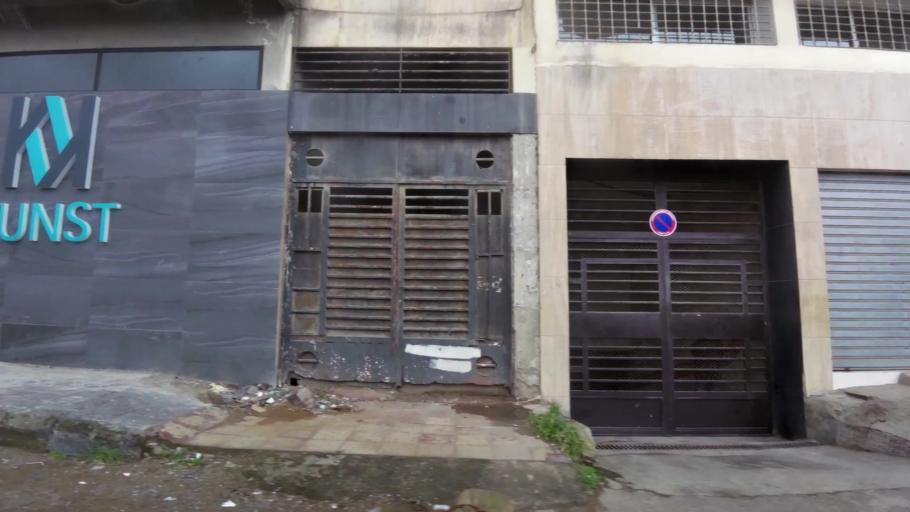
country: MA
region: Grand Casablanca
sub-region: Casablanca
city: Casablanca
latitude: 33.6006
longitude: -7.6483
